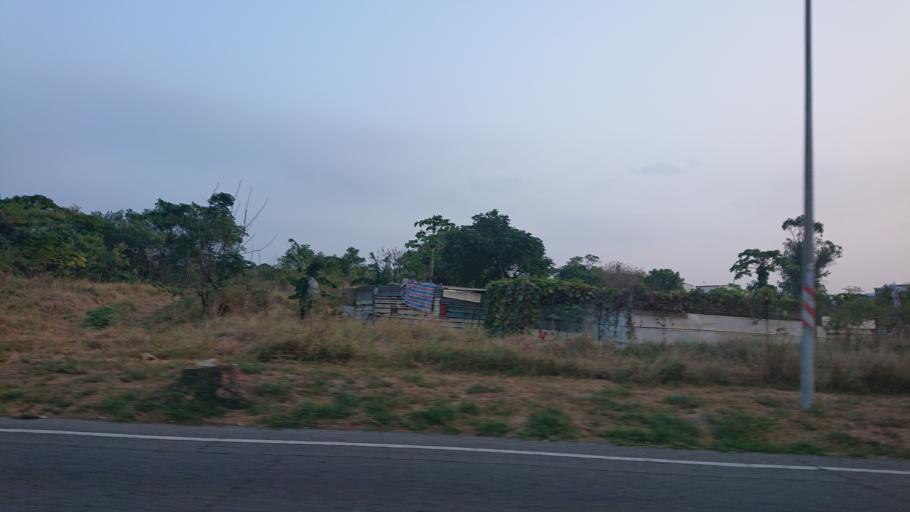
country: TW
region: Fukien
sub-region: Kinmen
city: Jincheng
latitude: 24.4502
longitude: 118.3404
